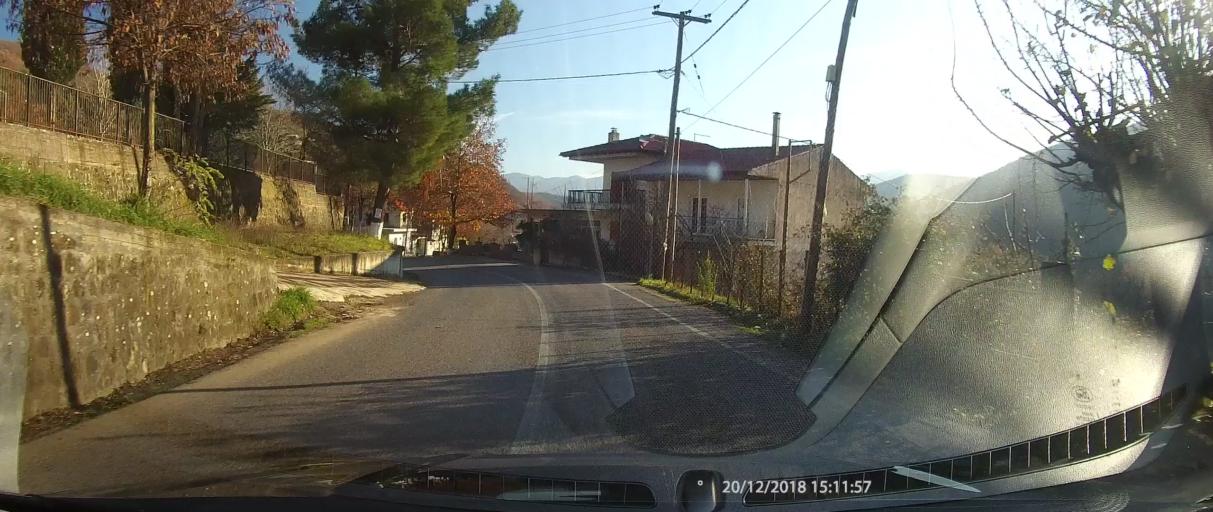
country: GR
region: Central Greece
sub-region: Nomos Fthiotidos
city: Makrakomi
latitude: 38.9452
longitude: 21.9601
